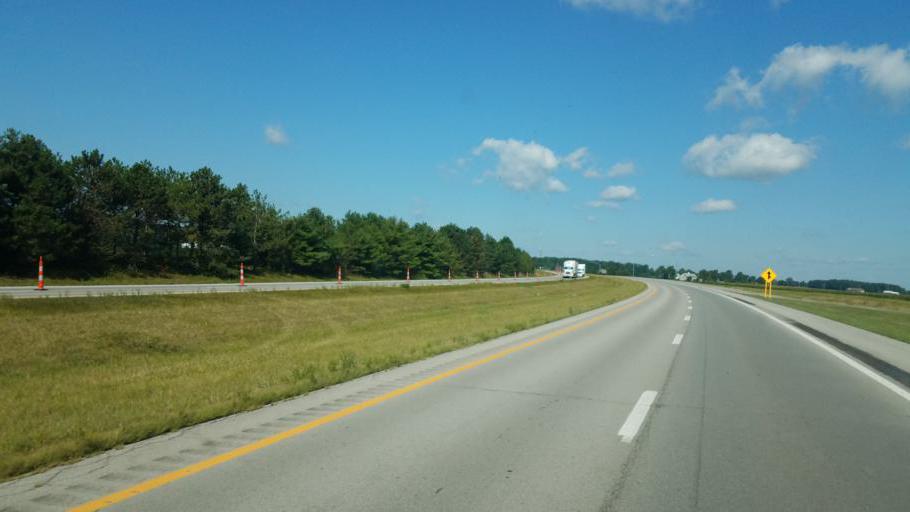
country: US
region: Ohio
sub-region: Wyandot County
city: Carey
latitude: 40.9222
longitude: -83.3582
